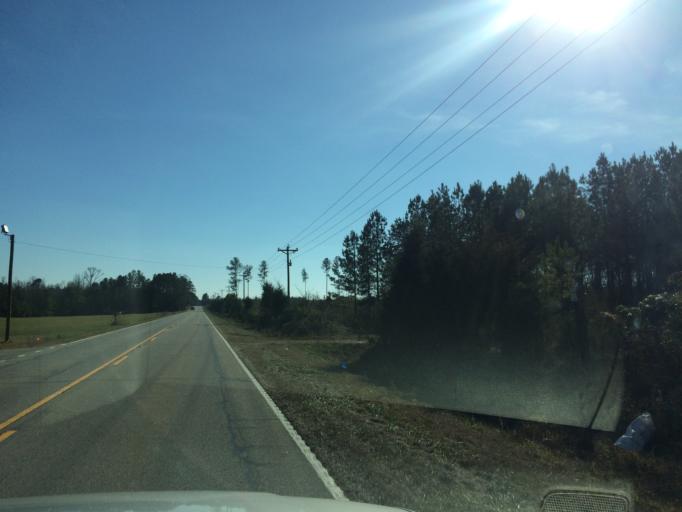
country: US
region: South Carolina
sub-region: Greenwood County
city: Ninety Six
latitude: 34.3120
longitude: -82.0486
